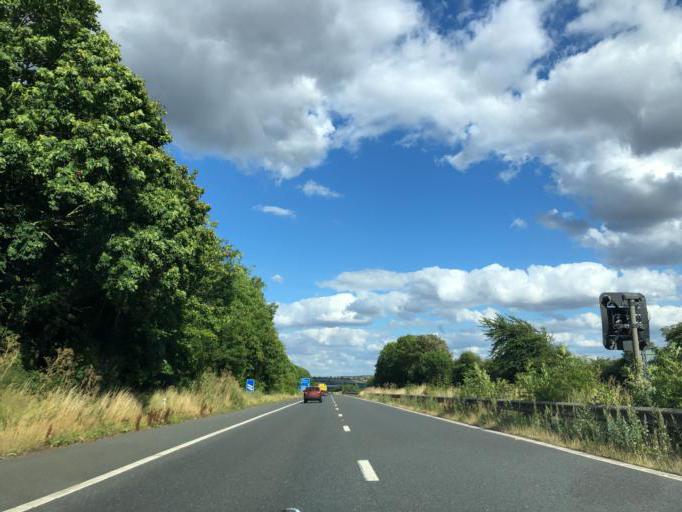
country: GB
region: England
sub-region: Warwickshire
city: Dunchurch
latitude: 52.3337
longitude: -1.2931
